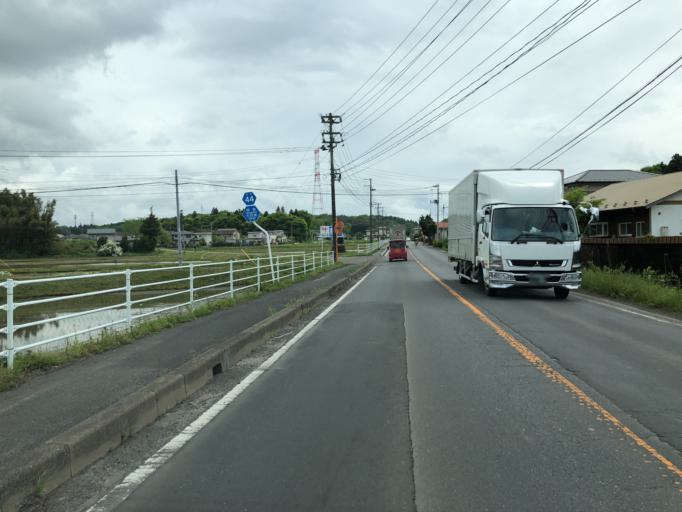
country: JP
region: Fukushima
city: Ishikawa
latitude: 37.0608
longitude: 140.3740
